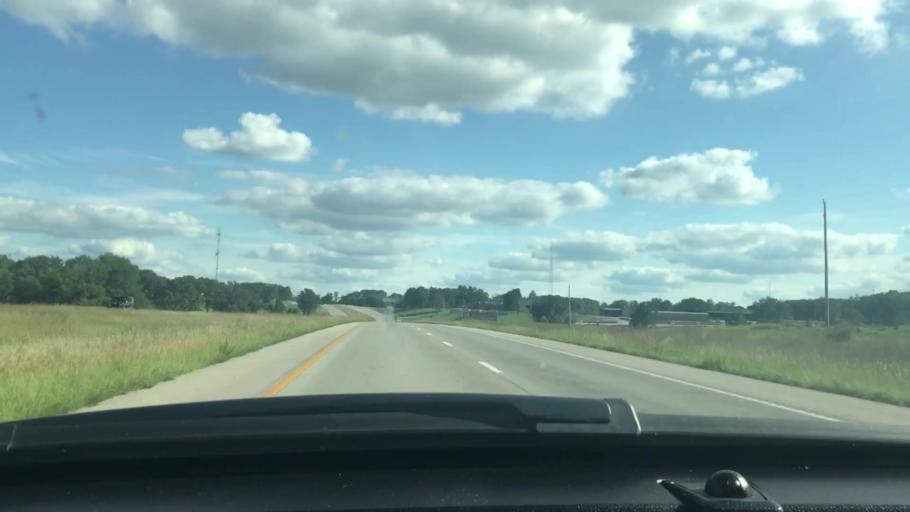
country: US
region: Missouri
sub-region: Howell County
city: West Plains
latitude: 36.8270
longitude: -91.9137
